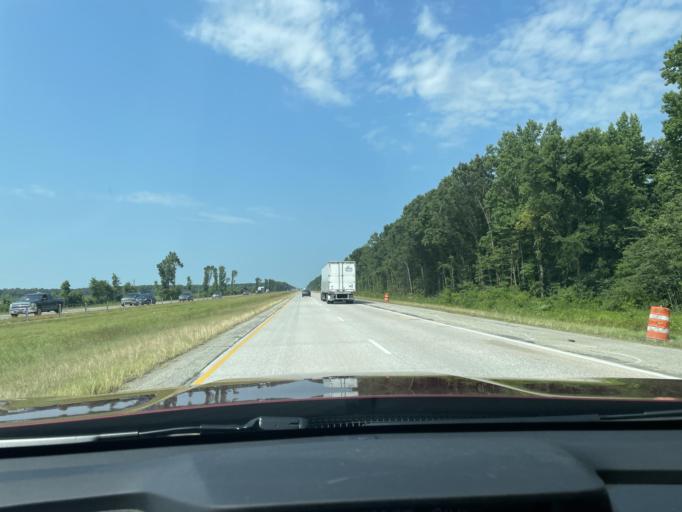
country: US
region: Arkansas
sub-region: White County
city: Beebe
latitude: 35.1493
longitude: -91.7950
